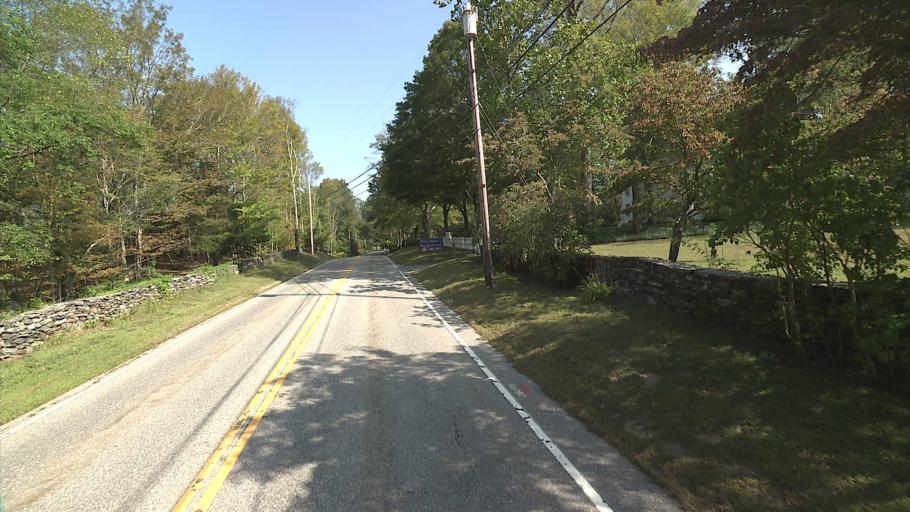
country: US
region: Connecticut
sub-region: Windham County
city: Plainfield Village
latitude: 41.6628
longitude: -71.9735
